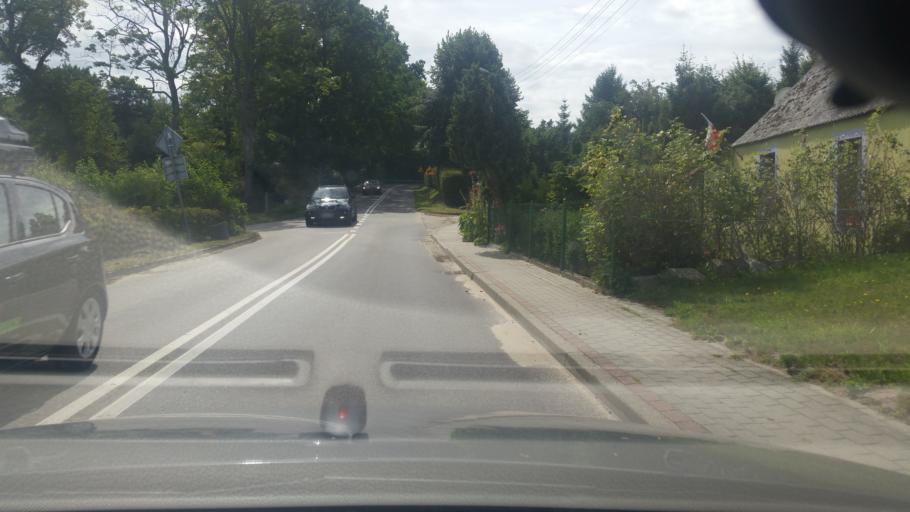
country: PL
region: Pomeranian Voivodeship
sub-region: Powiat wejherowski
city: Choczewo
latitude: 54.7589
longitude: 17.7519
